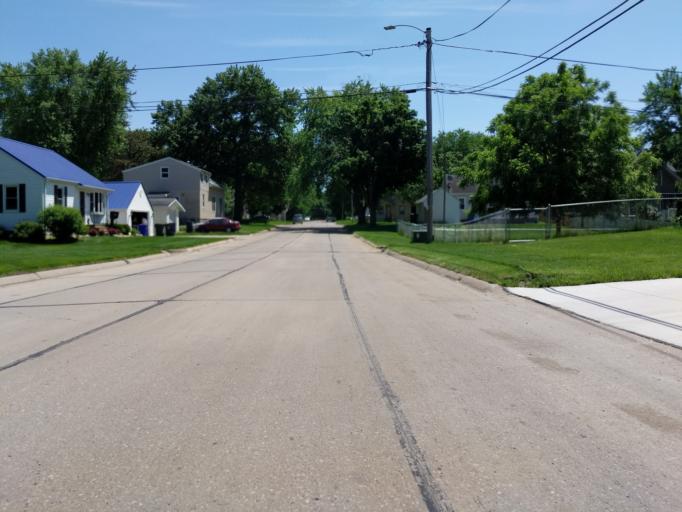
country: US
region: Iowa
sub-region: Linn County
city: Cedar Rapids
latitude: 42.0121
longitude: -91.6410
